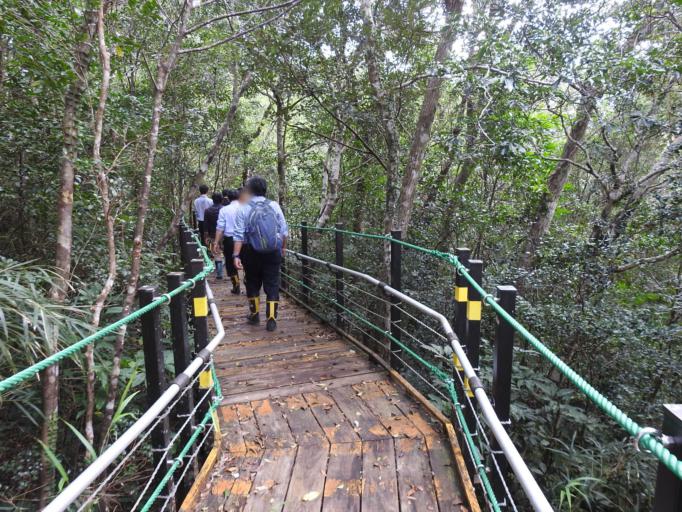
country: JP
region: Okinawa
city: Nago
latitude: 26.7210
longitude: 128.2659
